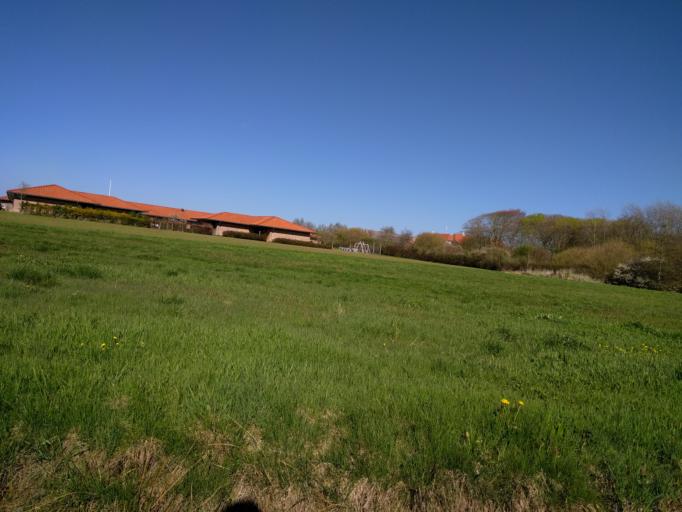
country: DK
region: Central Jutland
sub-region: Ringkobing-Skjern Kommune
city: Ringkobing
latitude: 56.0916
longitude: 8.2549
